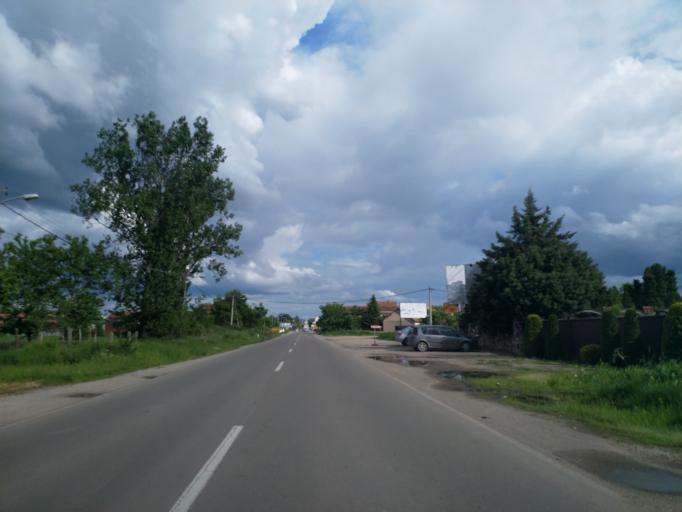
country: RS
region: Central Serbia
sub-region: Pomoravski Okrug
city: Paracin
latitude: 43.8750
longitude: 21.3963
